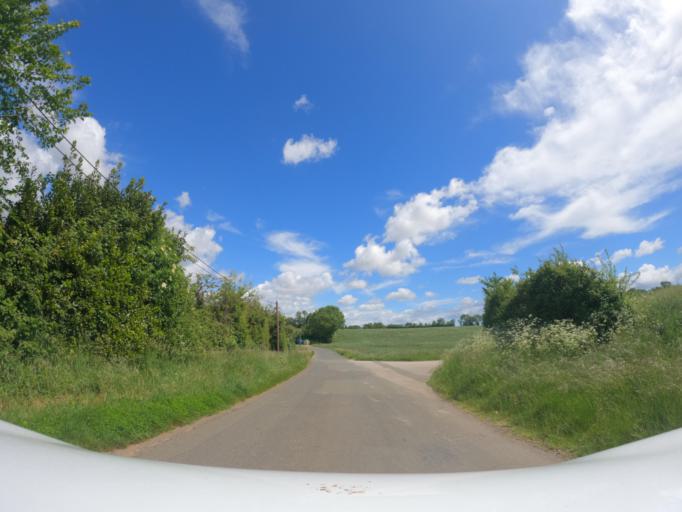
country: FR
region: Pays de la Loire
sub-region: Departement de la Vendee
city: Le Champ-Saint-Pere
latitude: 46.4910
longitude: -1.3348
